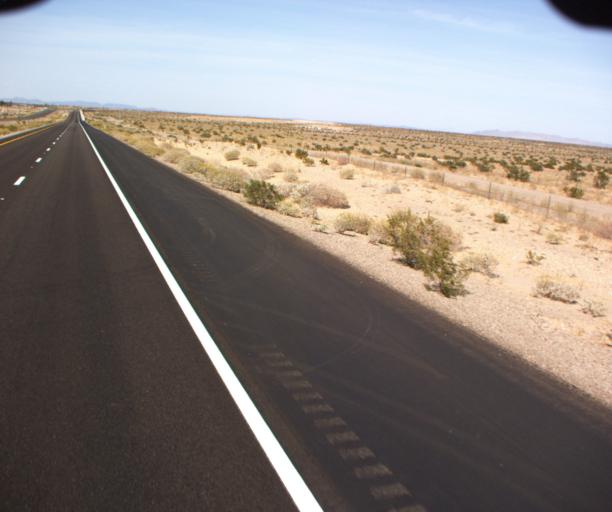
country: US
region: Arizona
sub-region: Yuma County
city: Somerton
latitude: 32.5443
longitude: -114.5620
